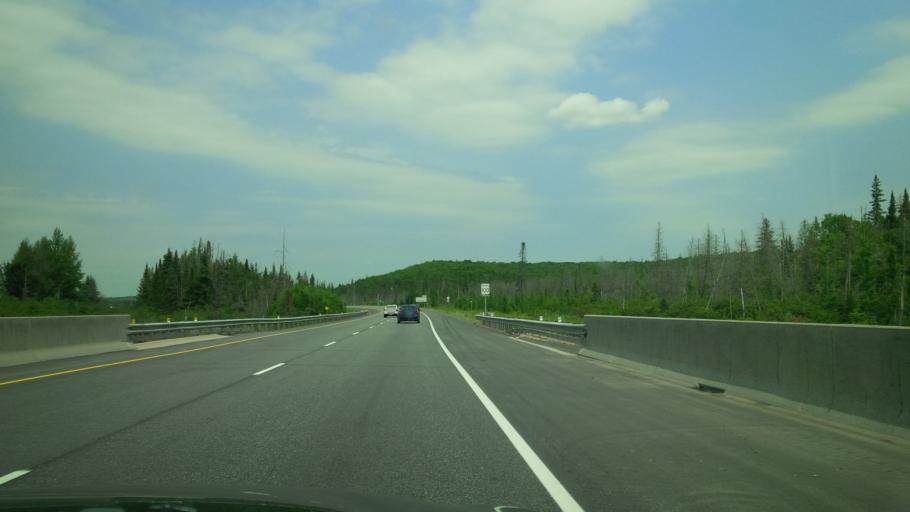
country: CA
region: Ontario
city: Huntsville
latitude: 45.4280
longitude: -79.2384
